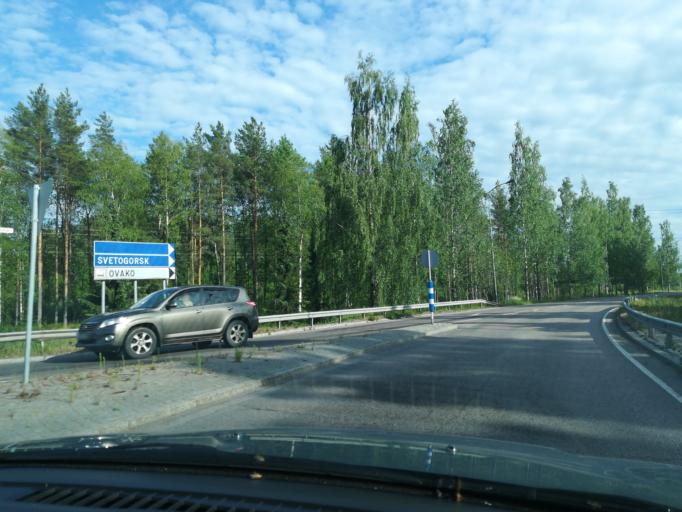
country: FI
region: South Karelia
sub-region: Imatra
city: Imatra
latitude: 61.1660
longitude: 28.7898
